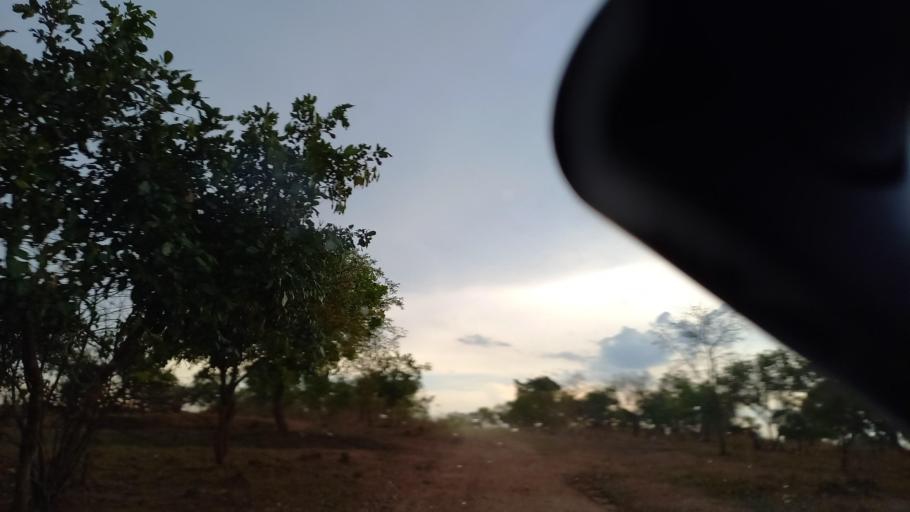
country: ZM
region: Lusaka
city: Kafue
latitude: -15.9872
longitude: 28.2665
